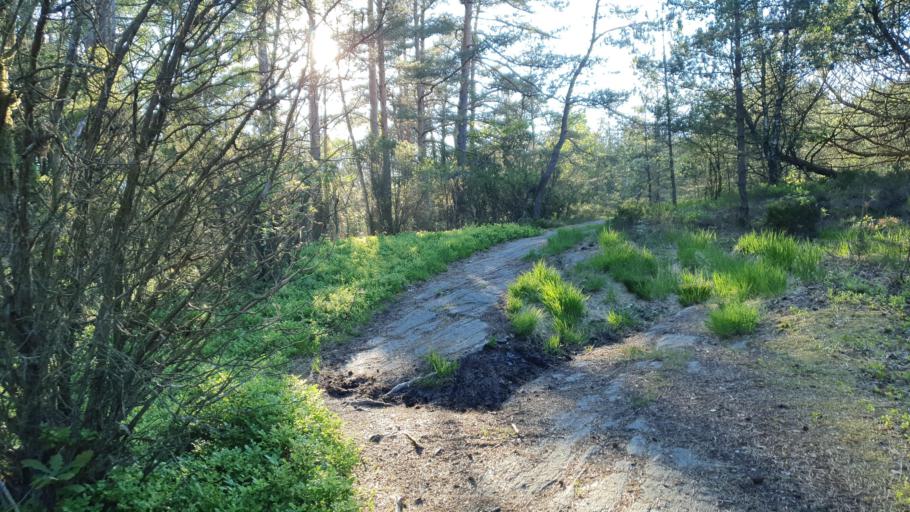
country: SE
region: Vaestra Goetaland
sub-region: Molndal
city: Kallered
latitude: 57.6326
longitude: 12.0591
